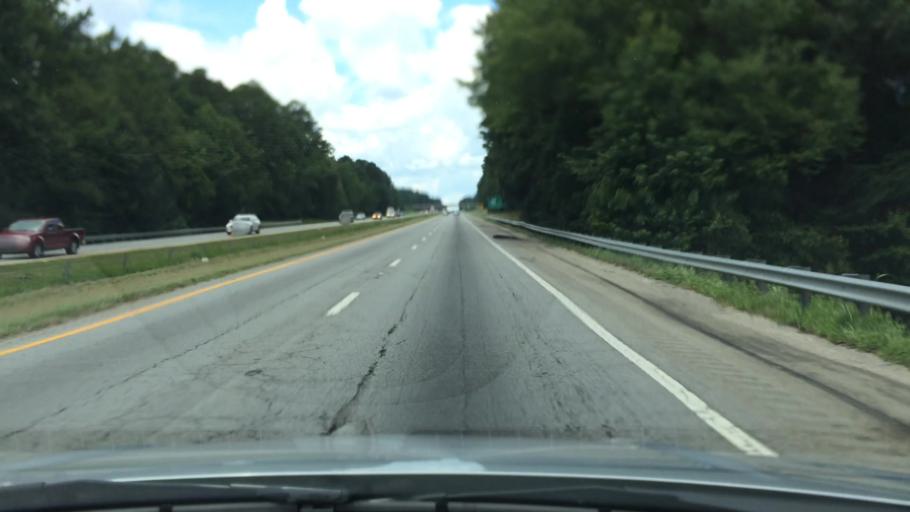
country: US
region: South Carolina
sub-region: Newberry County
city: Newberry
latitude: 34.3273
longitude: -81.6027
